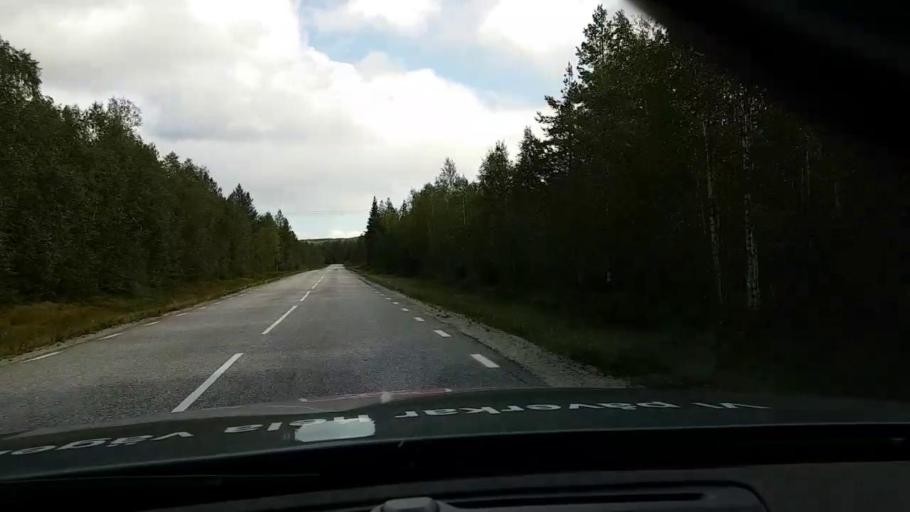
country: SE
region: Vaesternorrland
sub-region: OErnskoeldsviks Kommun
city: Bredbyn
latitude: 63.6766
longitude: 17.7924
